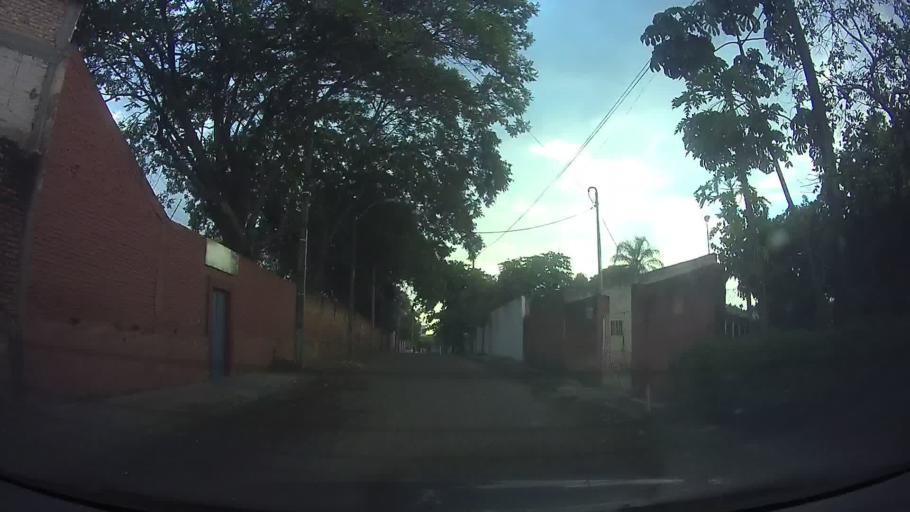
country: PY
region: Asuncion
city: Asuncion
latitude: -25.2649
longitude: -57.5799
